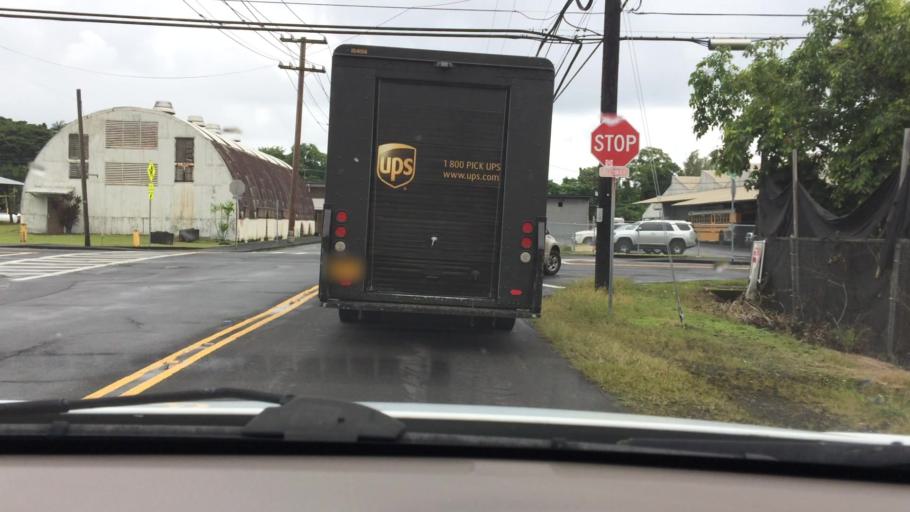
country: US
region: Hawaii
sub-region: Hawaii County
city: Hilo
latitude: 19.7210
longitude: -155.0657
